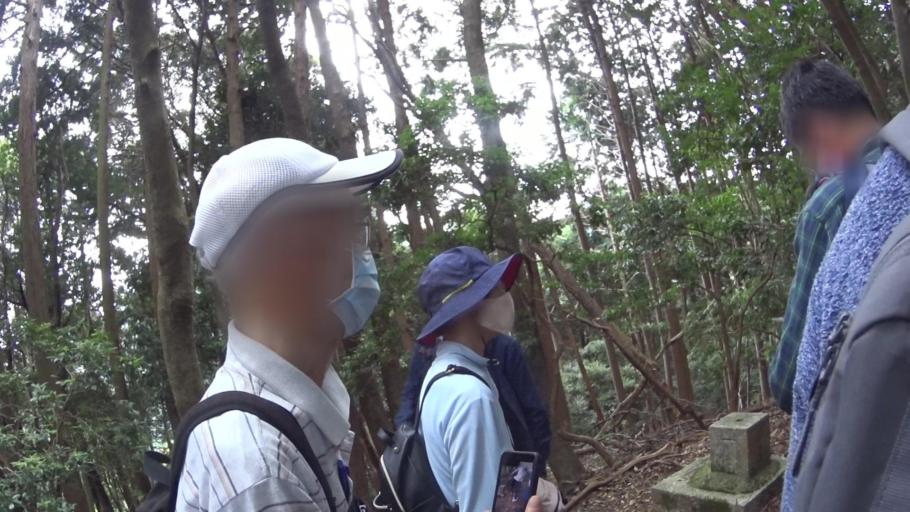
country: JP
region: Osaka
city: Kishiwada
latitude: 34.4924
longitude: 135.3249
